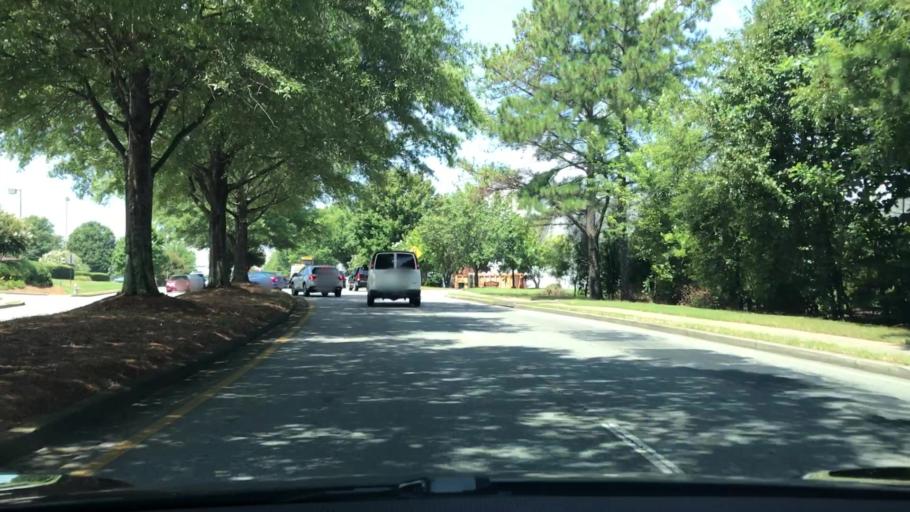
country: US
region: Georgia
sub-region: Fulton County
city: Johns Creek
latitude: 34.0713
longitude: -84.1641
